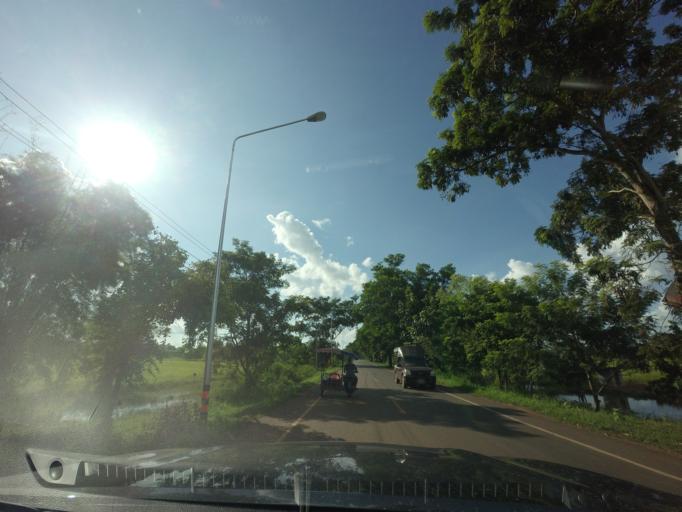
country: TH
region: Changwat Udon Thani
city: Ban Dung
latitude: 17.7395
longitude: 103.3455
